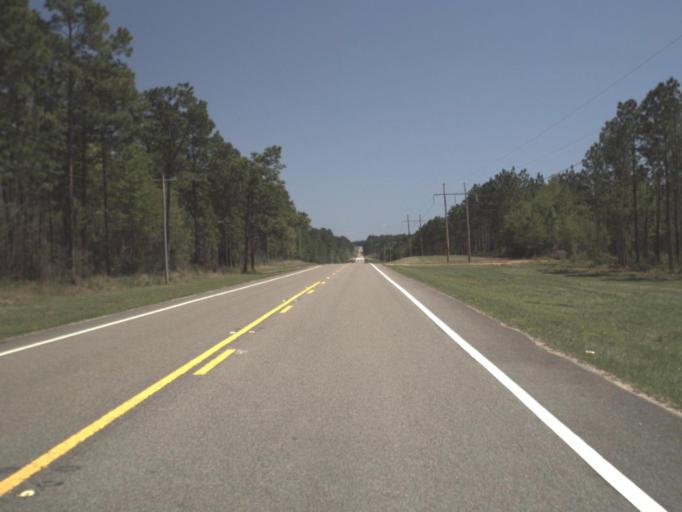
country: US
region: Florida
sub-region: Santa Rosa County
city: Point Baker
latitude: 30.8870
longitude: -86.9690
